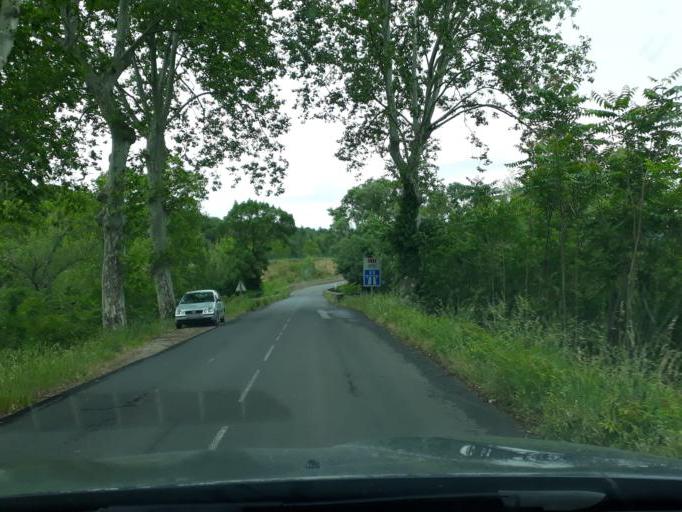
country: FR
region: Languedoc-Roussillon
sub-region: Departement de l'Herault
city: Lodeve
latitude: 43.7609
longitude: 3.3277
